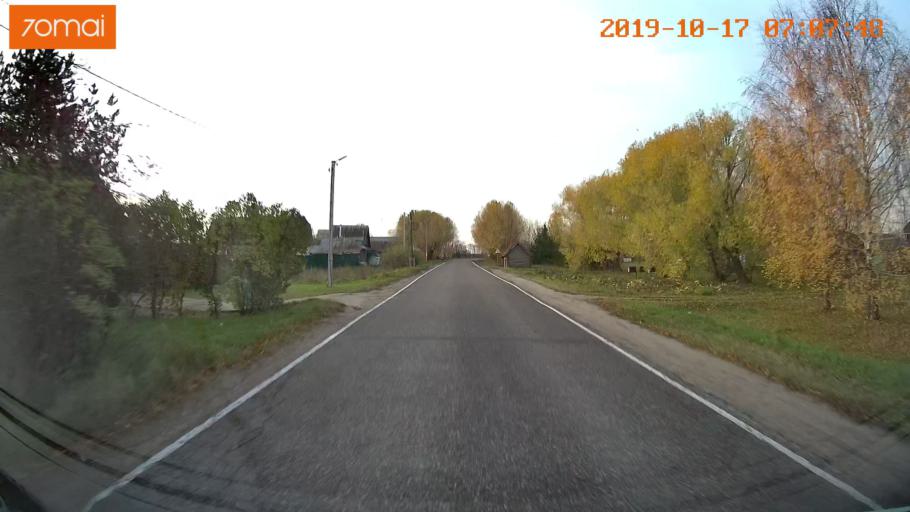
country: RU
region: Vladimir
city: Suzdal'
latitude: 56.4257
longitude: 40.4156
